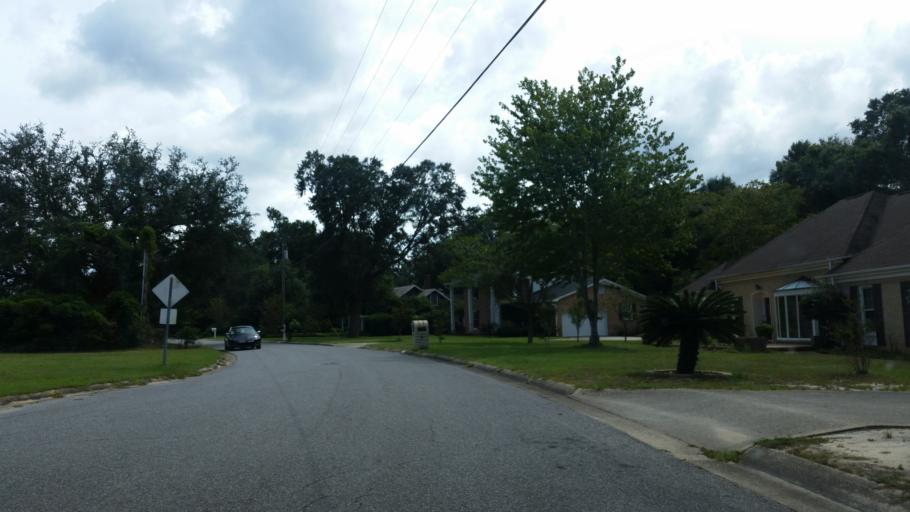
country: US
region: Florida
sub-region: Escambia County
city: Ferry Pass
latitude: 30.5423
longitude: -87.2366
